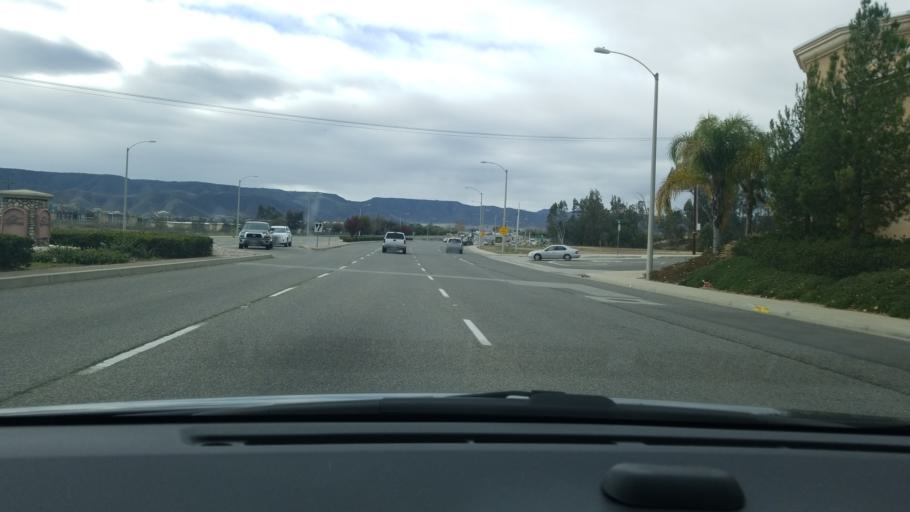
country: US
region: California
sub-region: Riverside County
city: Murrieta
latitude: 33.5556
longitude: -117.1863
